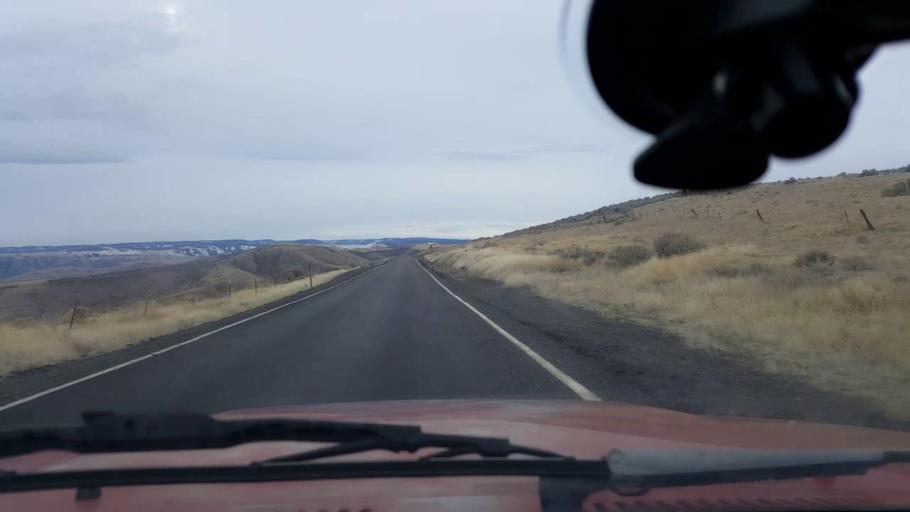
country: US
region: Washington
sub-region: Asotin County
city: Clarkston Heights-Vineland
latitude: 46.3374
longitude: -117.2777
